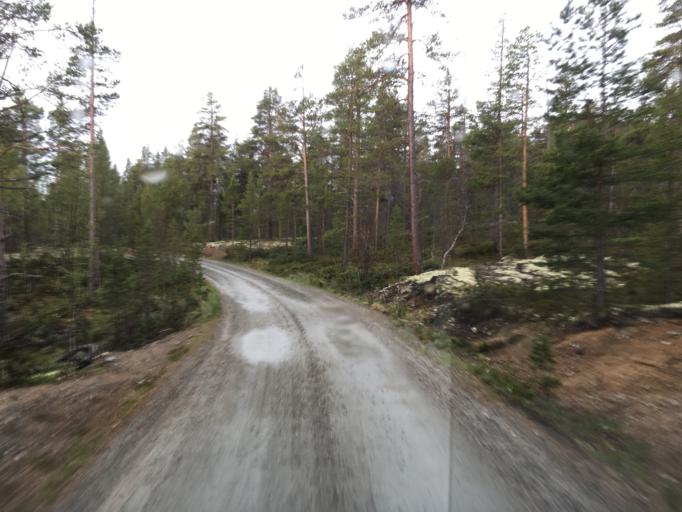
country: NO
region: Hedmark
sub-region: Folldal
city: Folldal
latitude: 62.0718
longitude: 9.9419
